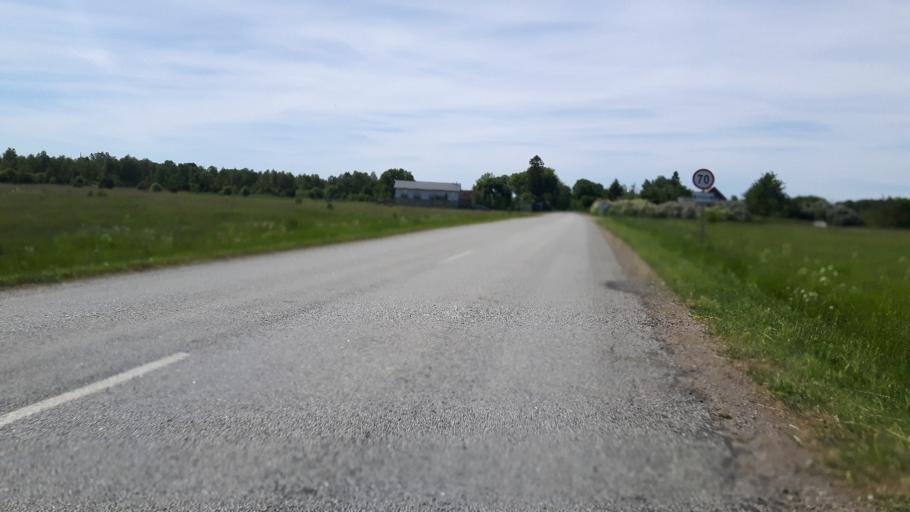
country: EE
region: Harju
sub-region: Kuusalu vald
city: Kuusalu
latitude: 59.4669
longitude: 25.3177
